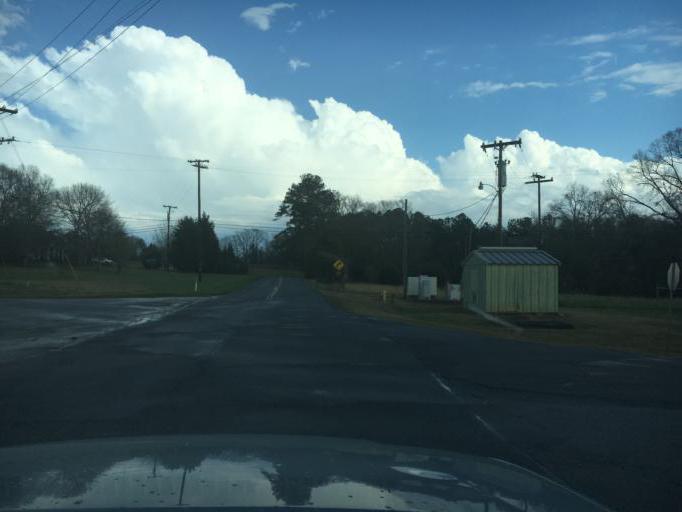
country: US
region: South Carolina
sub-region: Greenville County
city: Parker
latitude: 34.8626
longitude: -82.5045
